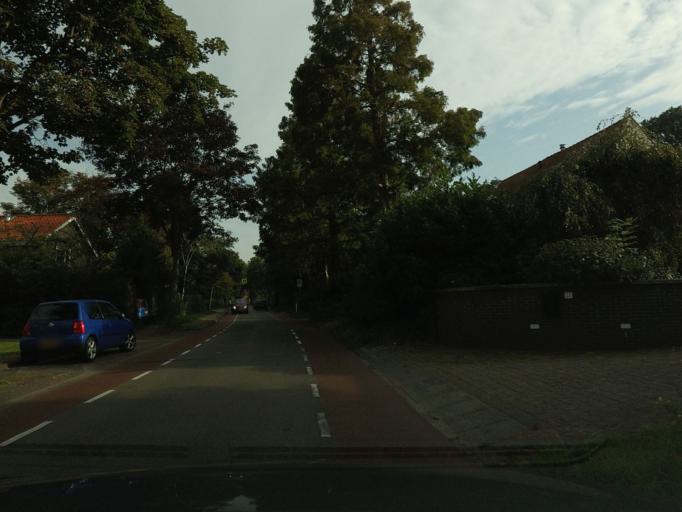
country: NL
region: North Holland
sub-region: Gemeente Schagen
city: Harenkarspel
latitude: 52.7070
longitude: 4.7014
